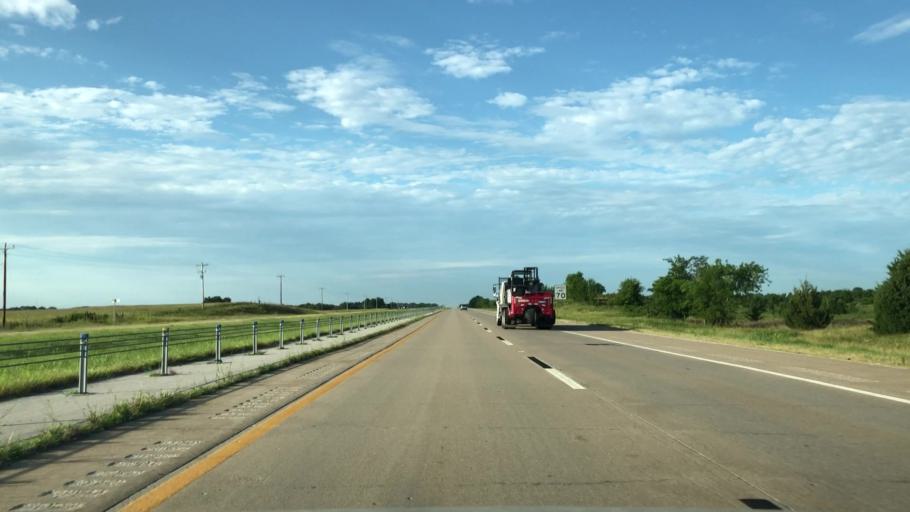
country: US
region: Oklahoma
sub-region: Osage County
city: Skiatook
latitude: 36.4519
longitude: -95.9208
